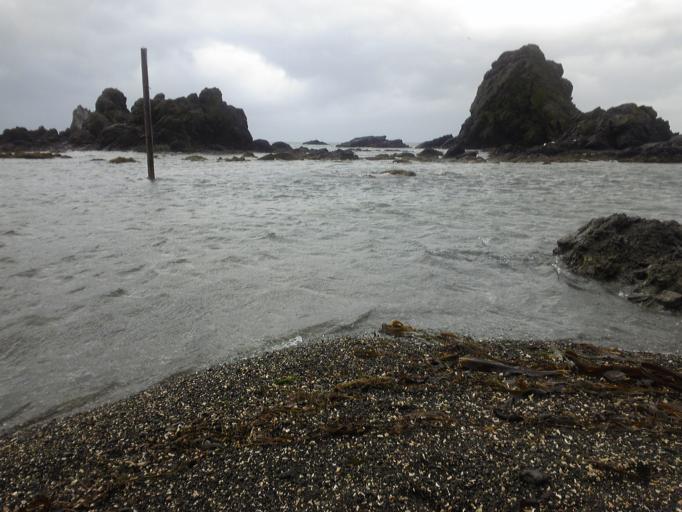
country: JP
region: Hokkaido
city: Shizunai-furukawacho
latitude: 41.9246
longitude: 143.2490
